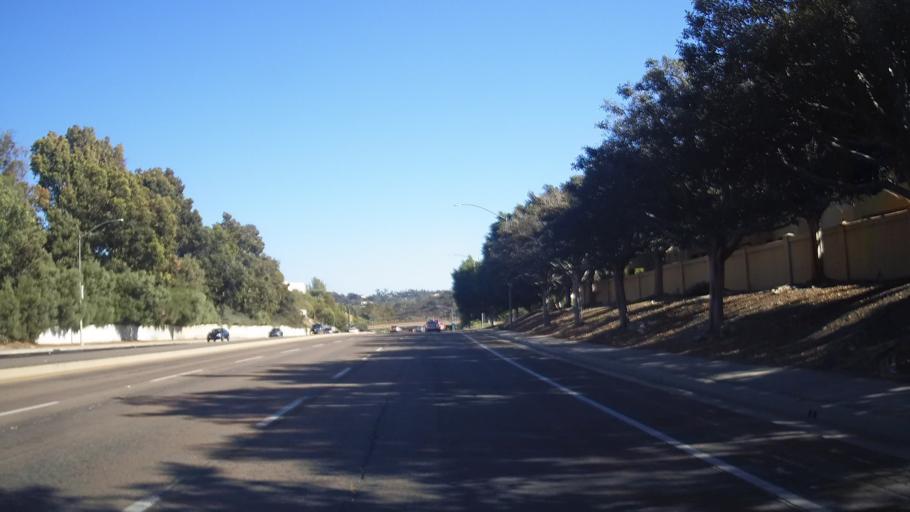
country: US
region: California
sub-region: San Diego County
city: Poway
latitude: 33.0075
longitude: -117.0945
